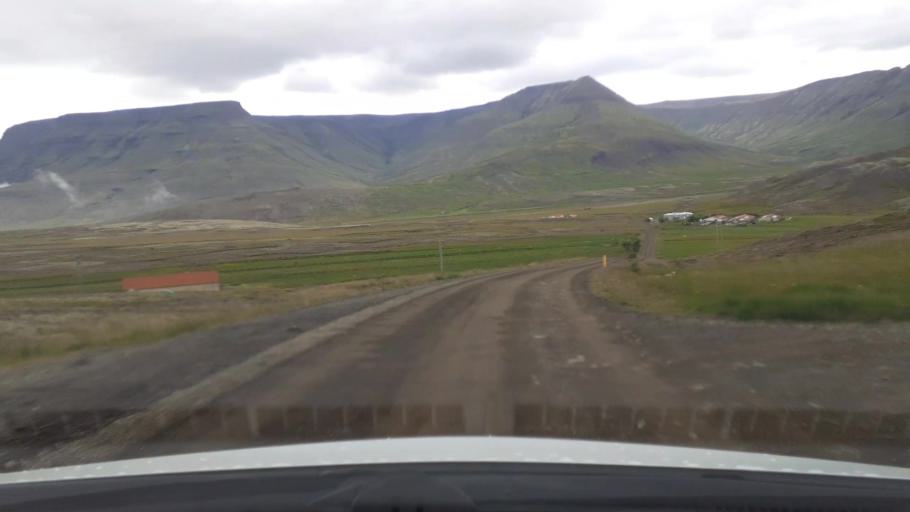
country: IS
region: Capital Region
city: Mosfellsbaer
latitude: 64.1981
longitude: -21.5570
